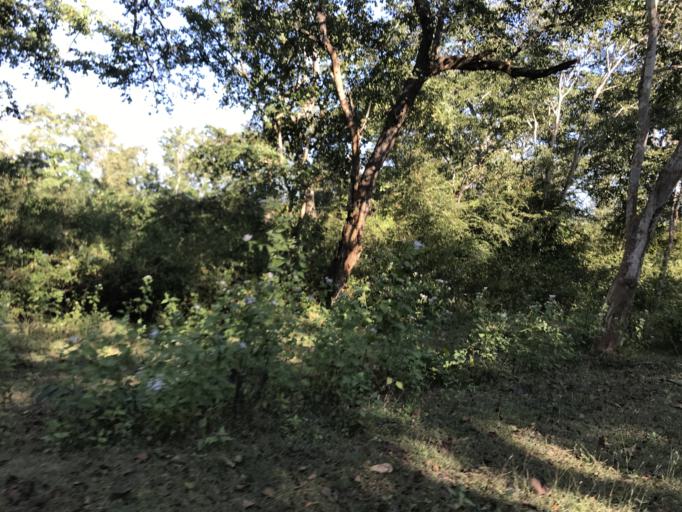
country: IN
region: Karnataka
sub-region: Mysore
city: Heggadadevankote
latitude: 11.9734
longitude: 76.2423
